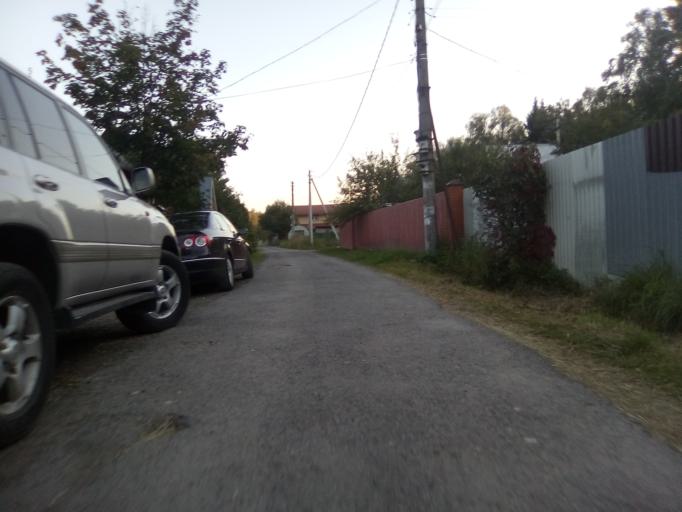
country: RU
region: Moskovskaya
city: Krasnoznamensk
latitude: 55.5639
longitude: 37.0289
